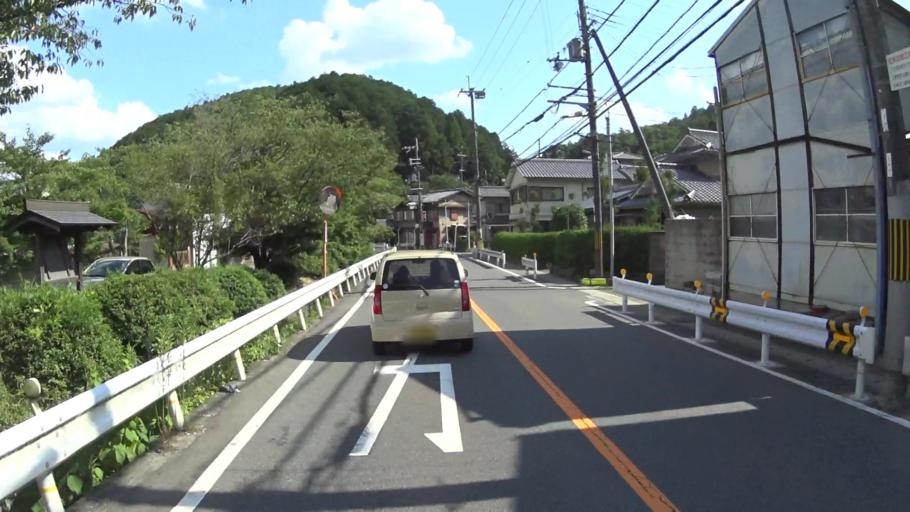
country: JP
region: Kyoto
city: Kyoto
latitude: 35.0386
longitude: 135.6880
